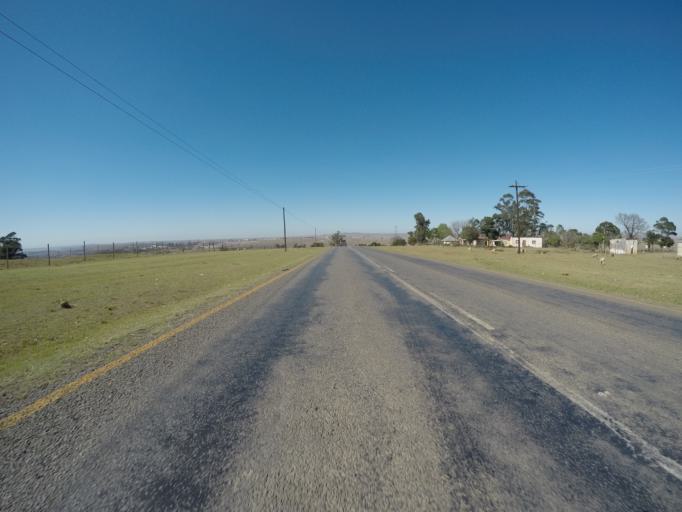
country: ZA
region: Eastern Cape
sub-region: OR Tambo District Municipality
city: Mthatha
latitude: -31.7923
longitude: 28.7452
